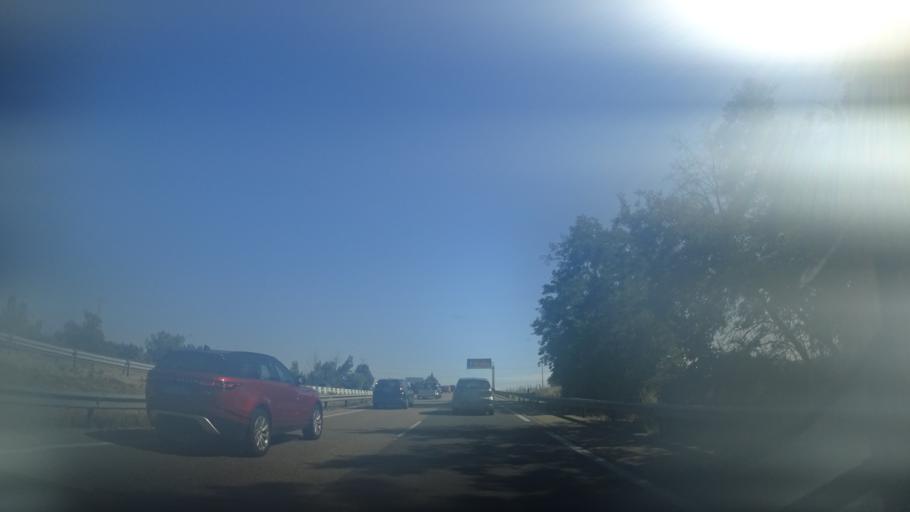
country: ES
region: Castille and Leon
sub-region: Provincia de Valladolid
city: Tordesillas
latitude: 41.4721
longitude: -4.9892
